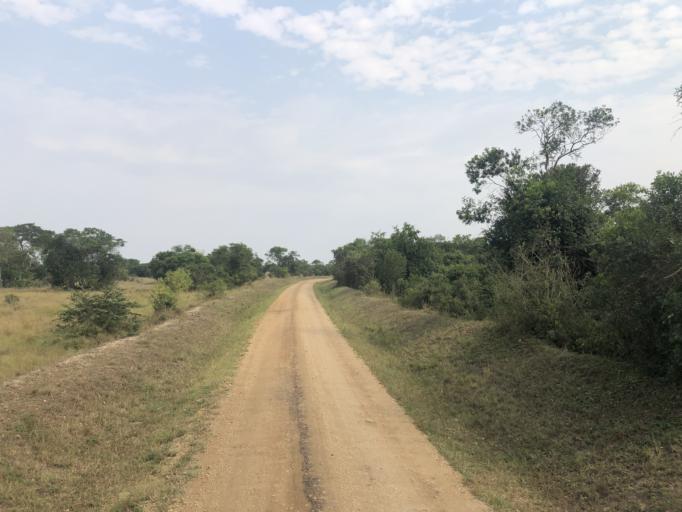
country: UG
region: Western Region
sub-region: Rubirizi District
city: Rubirizi
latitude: -0.4222
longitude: 29.7801
